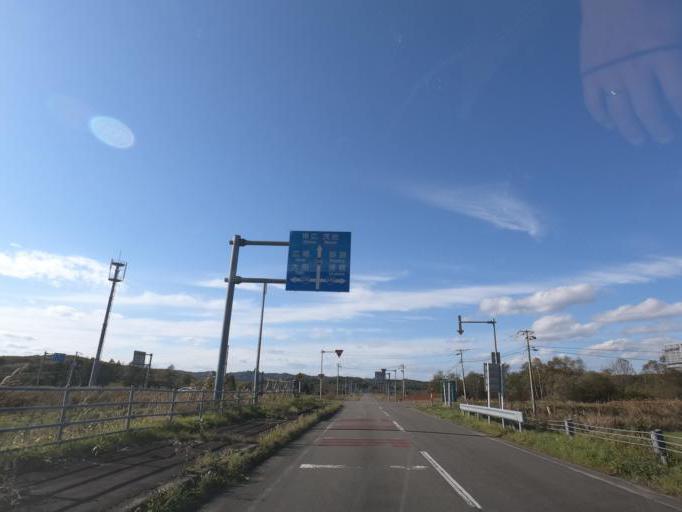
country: JP
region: Hokkaido
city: Obihiro
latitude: 42.6412
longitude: 143.5069
